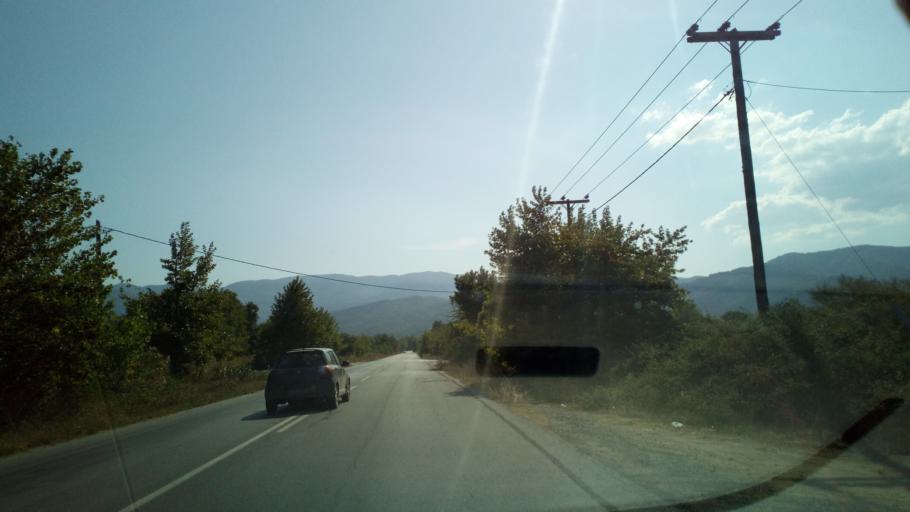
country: GR
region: Central Macedonia
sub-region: Nomos Thessalonikis
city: Stavros
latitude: 40.6057
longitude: 23.7749
